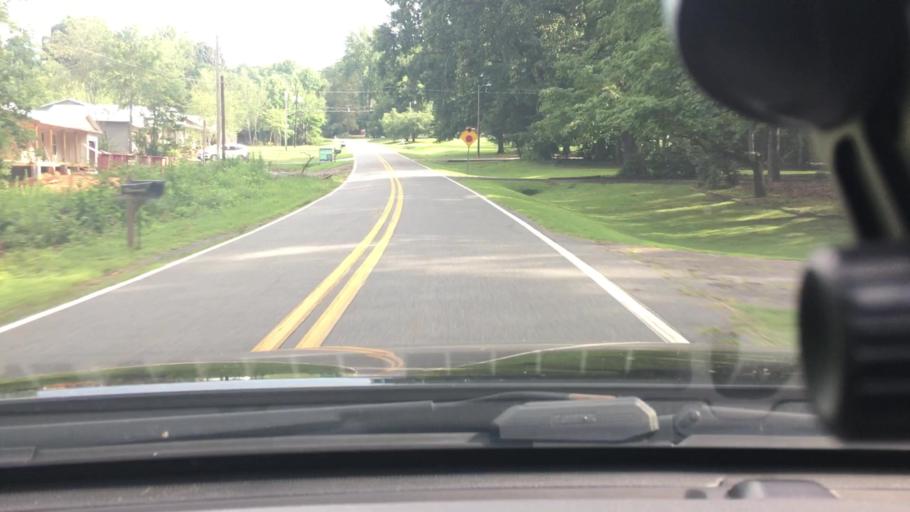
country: US
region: North Carolina
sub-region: Rutherford County
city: Rutherfordton
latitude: 35.3897
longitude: -81.9707
